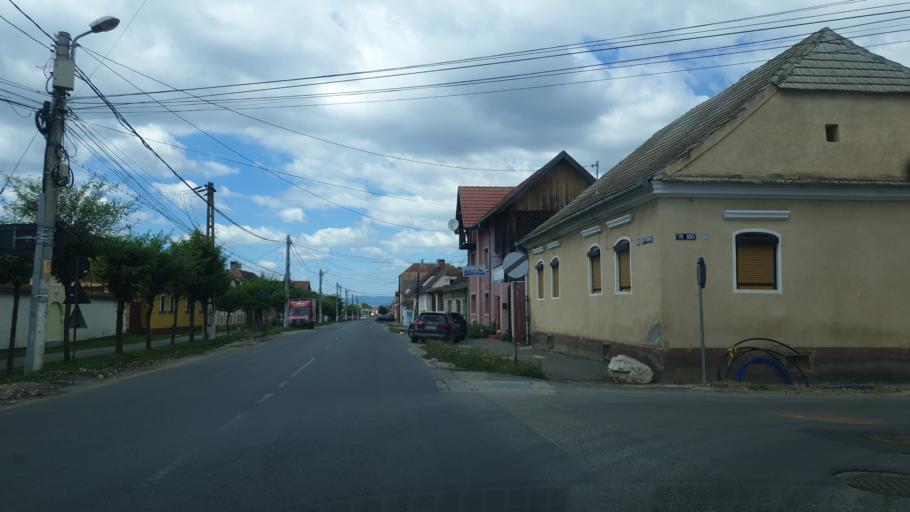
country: RO
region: Brasov
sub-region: Comuna Sanpetru
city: Sanpetru
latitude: 45.7122
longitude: 25.6336
